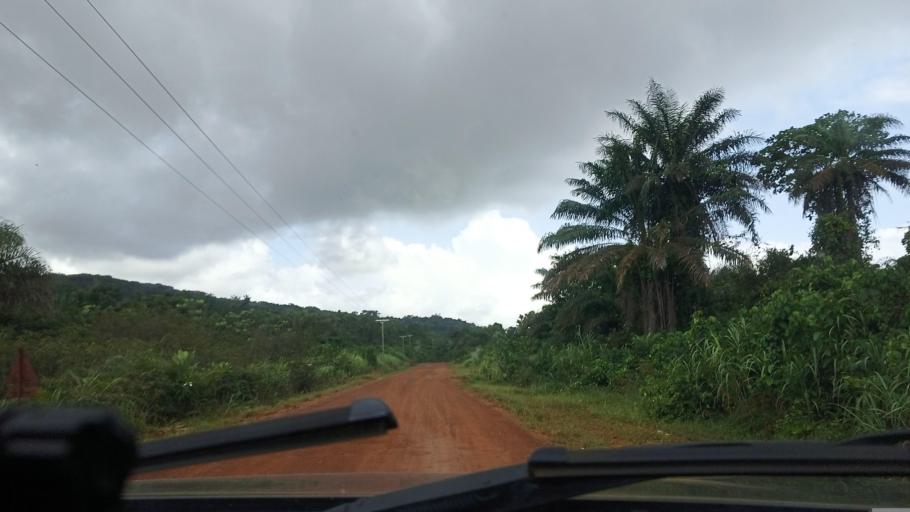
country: LR
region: Grand Cape Mount
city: Robertsport
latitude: 6.7082
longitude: -11.3344
